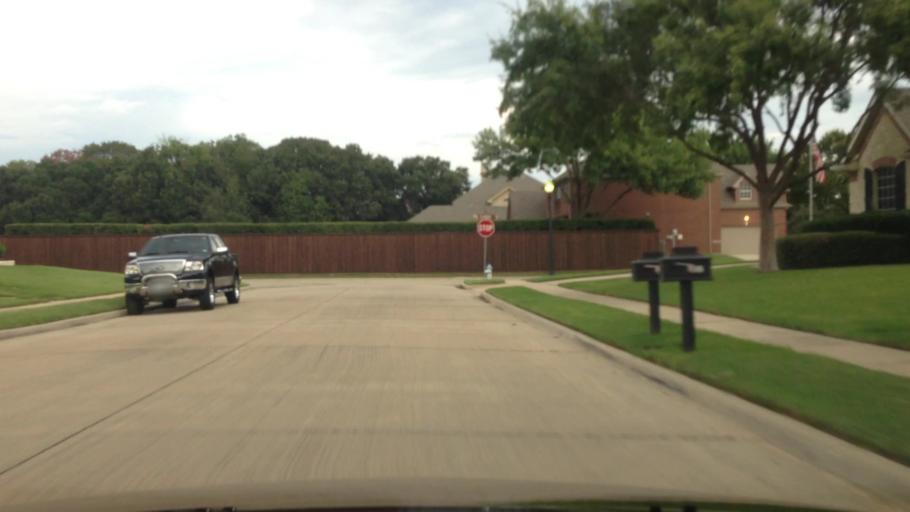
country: US
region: Texas
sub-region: Dallas County
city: Coppell
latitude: 33.0042
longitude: -97.0413
